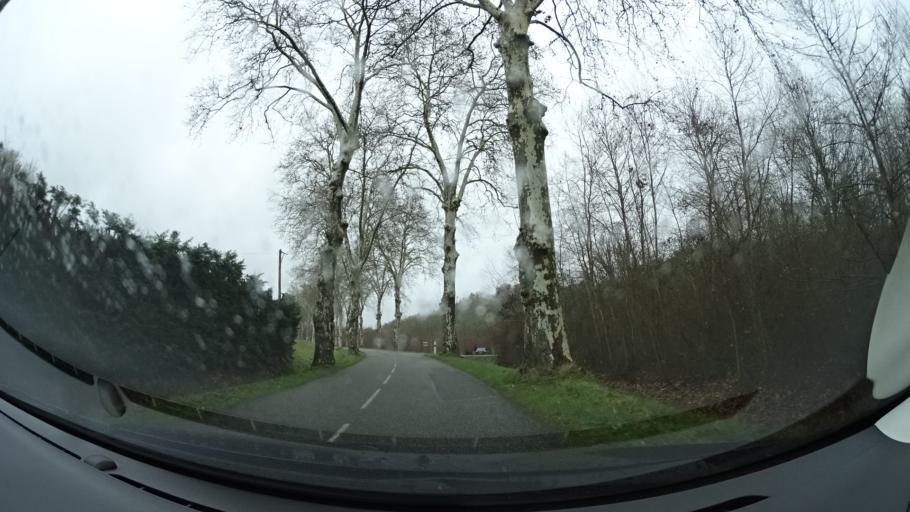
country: FR
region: Midi-Pyrenees
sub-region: Departement du Tarn-et-Garonne
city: Moissac
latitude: 44.1636
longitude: 1.1109
